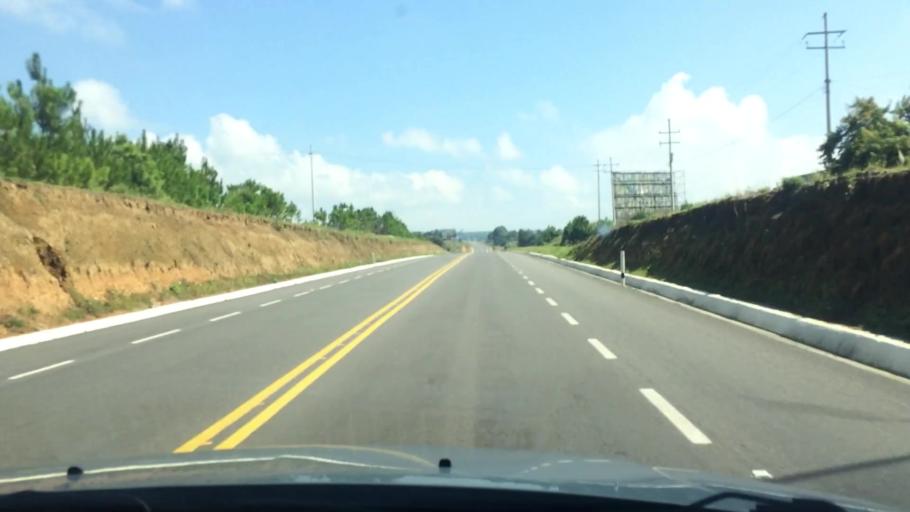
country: MX
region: Mexico
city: Amanalco de Becerra
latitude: 19.3055
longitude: -100.0091
